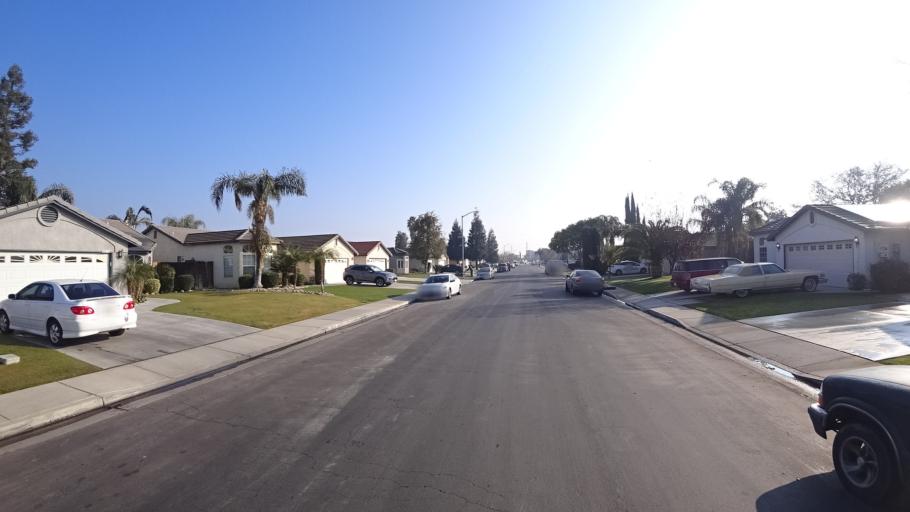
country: US
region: California
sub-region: Kern County
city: Greenacres
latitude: 35.3893
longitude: -119.1004
